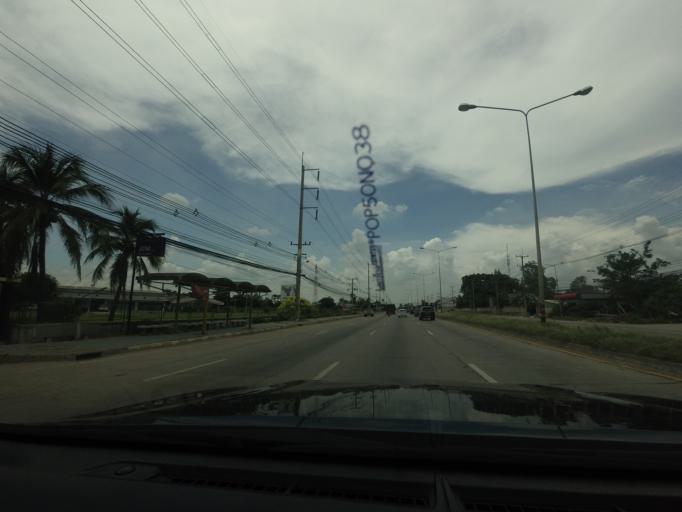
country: TH
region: Nakhon Pathom
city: Nakhon Pathom
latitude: 13.8602
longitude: 100.0109
